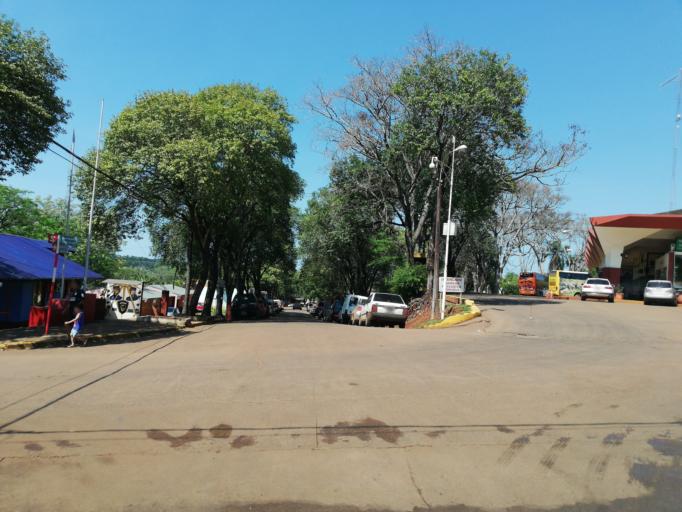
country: AR
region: Misiones
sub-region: Departamento de Eldorado
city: Eldorado
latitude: -26.4108
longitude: -54.6061
